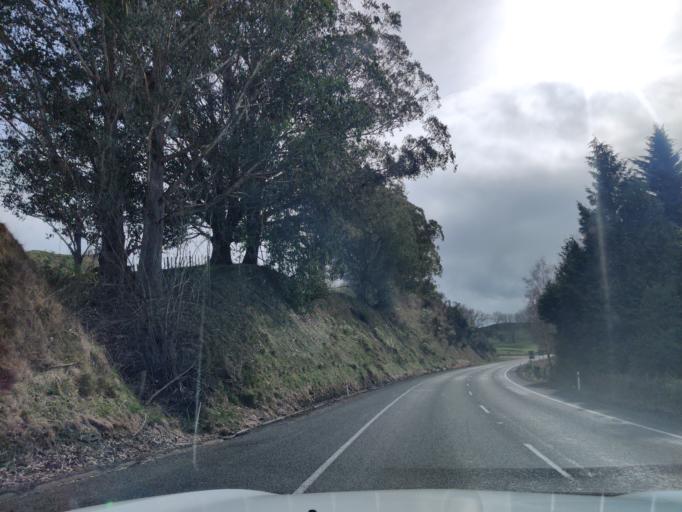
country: NZ
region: Manawatu-Wanganui
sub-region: Ruapehu District
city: Waiouru
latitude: -39.7450
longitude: 175.8348
